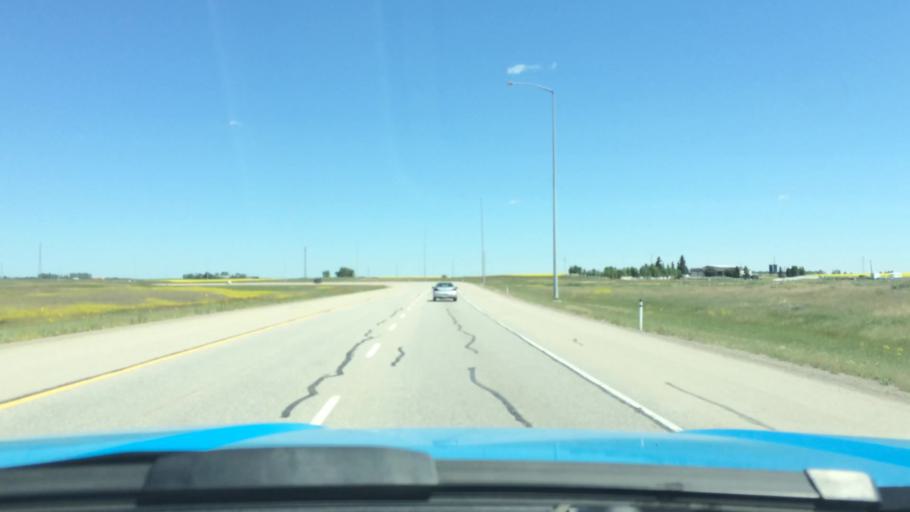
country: CA
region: Alberta
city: Chestermere
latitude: 51.1680
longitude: -113.9157
